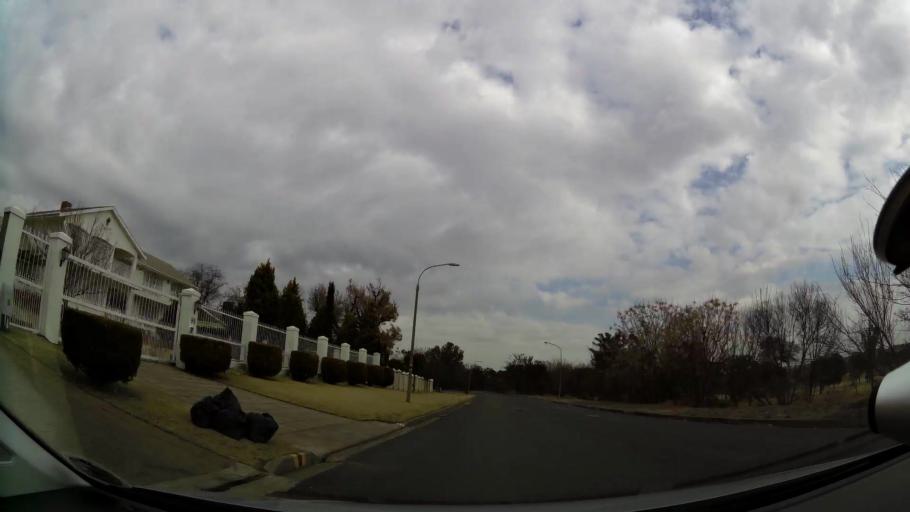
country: ZA
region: Orange Free State
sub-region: Fezile Dabi District Municipality
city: Kroonstad
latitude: -27.6691
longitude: 27.2473
